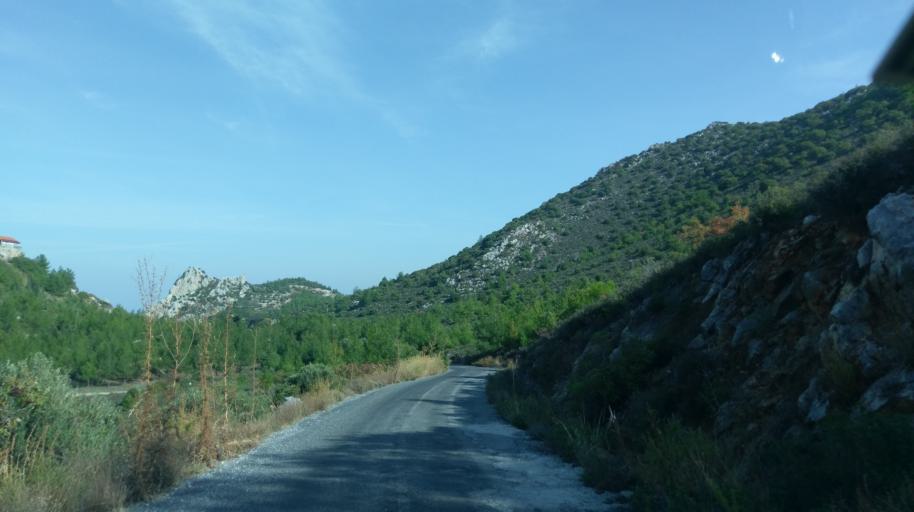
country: CY
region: Keryneia
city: Kyrenia
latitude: 35.3091
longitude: 33.2785
